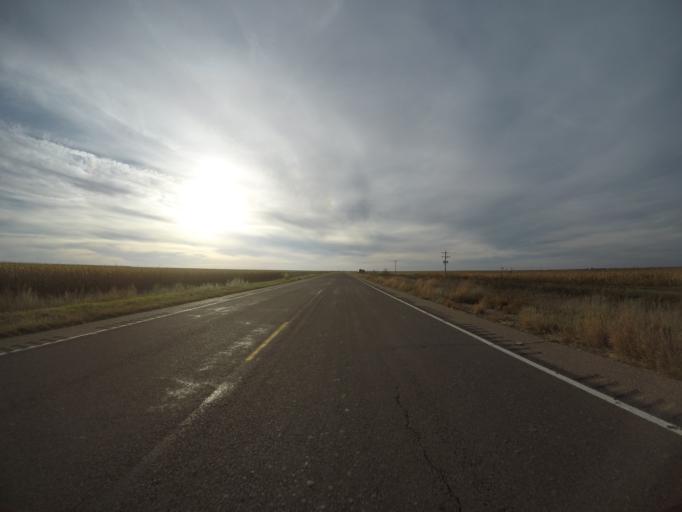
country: US
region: Colorado
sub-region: Kit Carson County
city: Burlington
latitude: 39.6578
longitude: -102.4746
